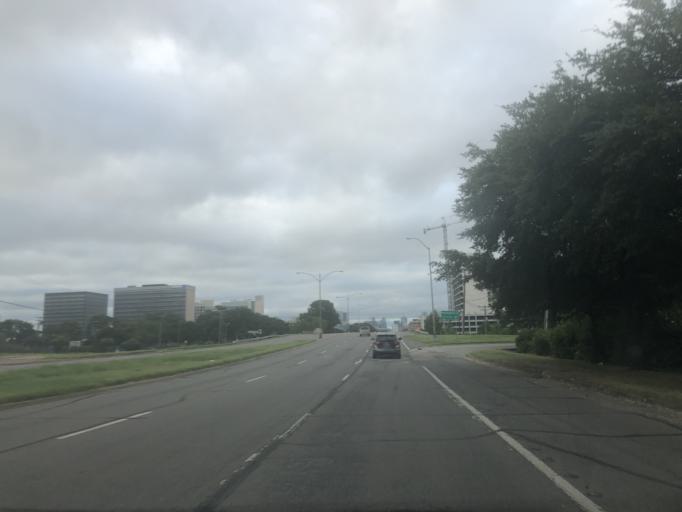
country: US
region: Texas
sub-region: Dallas County
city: University Park
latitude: 32.8238
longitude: -96.8523
